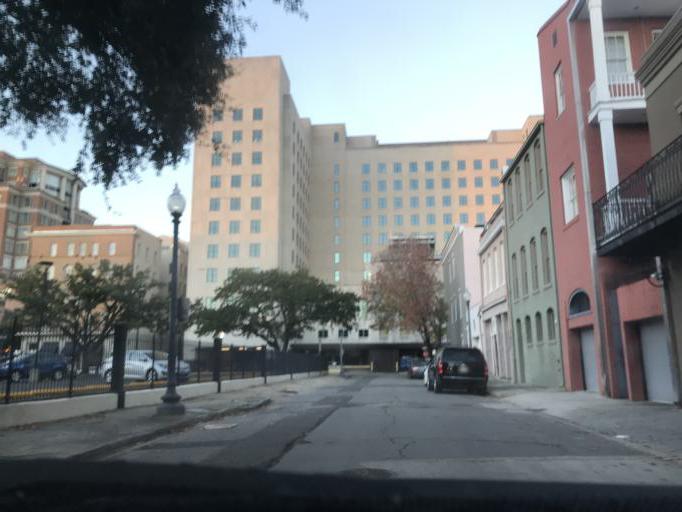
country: US
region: Louisiana
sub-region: Orleans Parish
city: New Orleans
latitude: 29.9466
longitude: -90.0709
